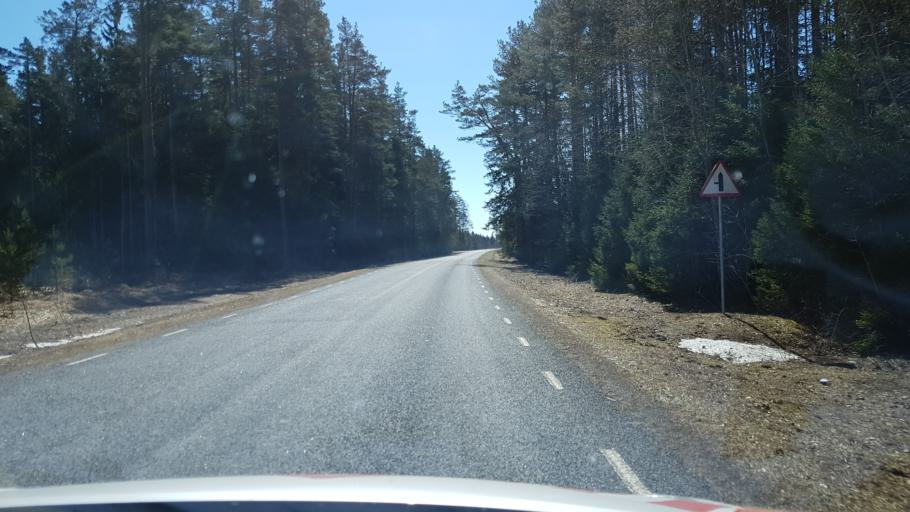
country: EE
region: Laeaene-Virumaa
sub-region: Haljala vald
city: Haljala
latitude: 59.4963
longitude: 26.2426
